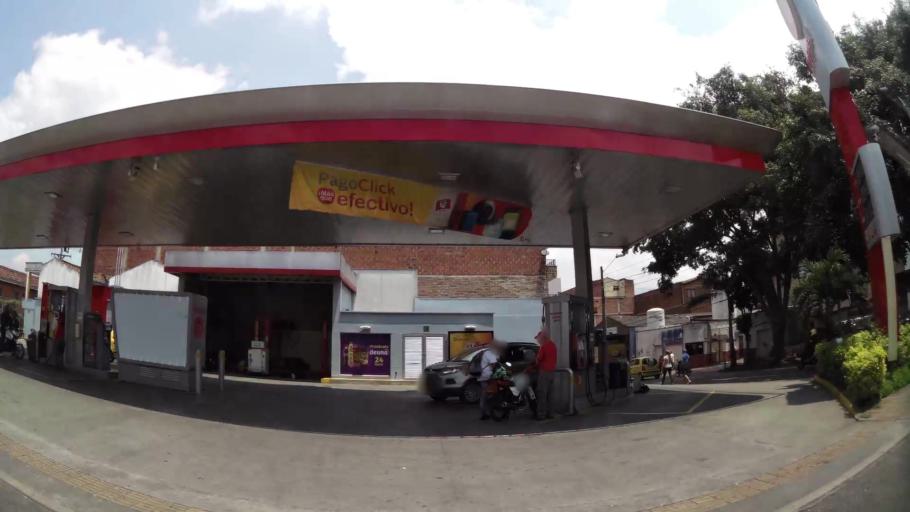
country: CO
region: Antioquia
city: Sabaneta
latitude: 6.1703
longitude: -75.6132
